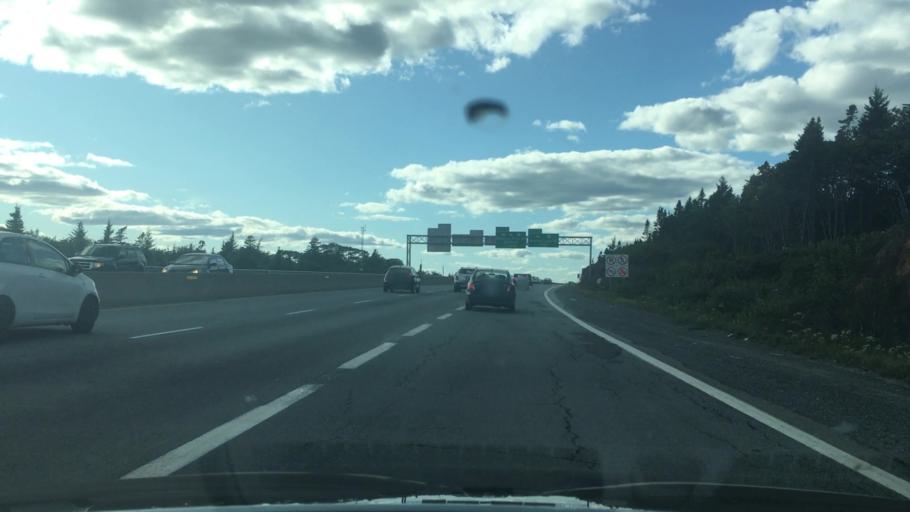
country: CA
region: Nova Scotia
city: Dartmouth
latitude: 44.6448
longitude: -63.6602
